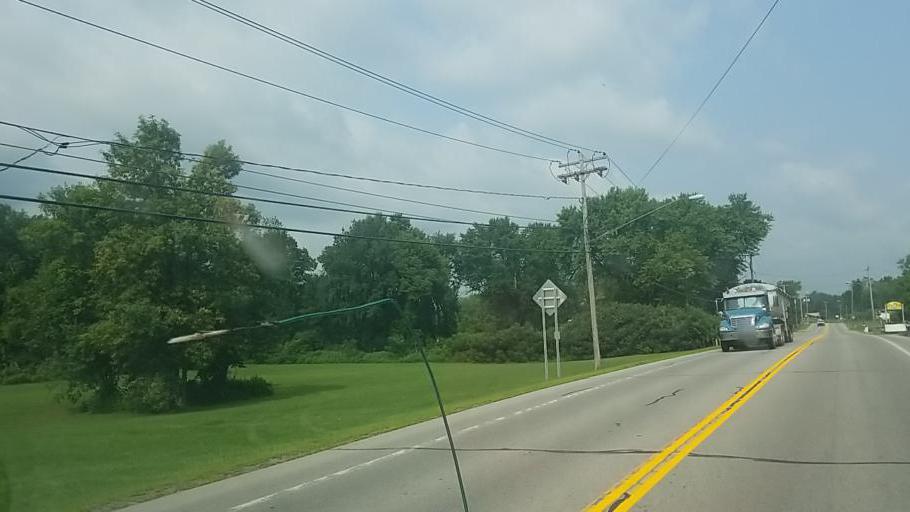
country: US
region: New York
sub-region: Montgomery County
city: Canajoharie
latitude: 42.9181
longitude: -74.5940
